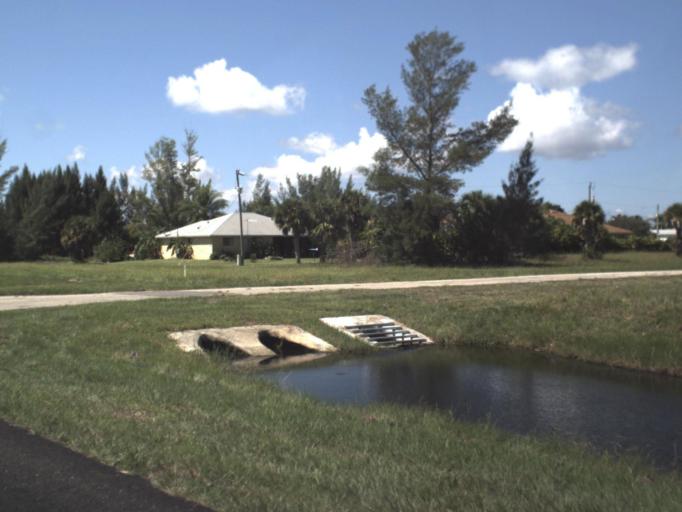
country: US
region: Florida
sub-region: Lee County
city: Pine Island Center
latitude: 26.6376
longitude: -82.0409
